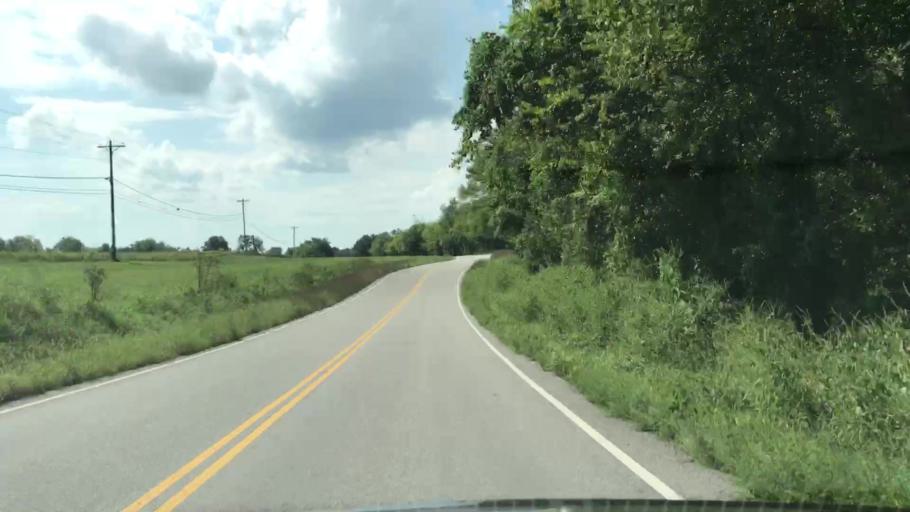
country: US
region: Tennessee
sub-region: Trousdale County
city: Hartsville
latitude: 36.4189
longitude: -86.1809
